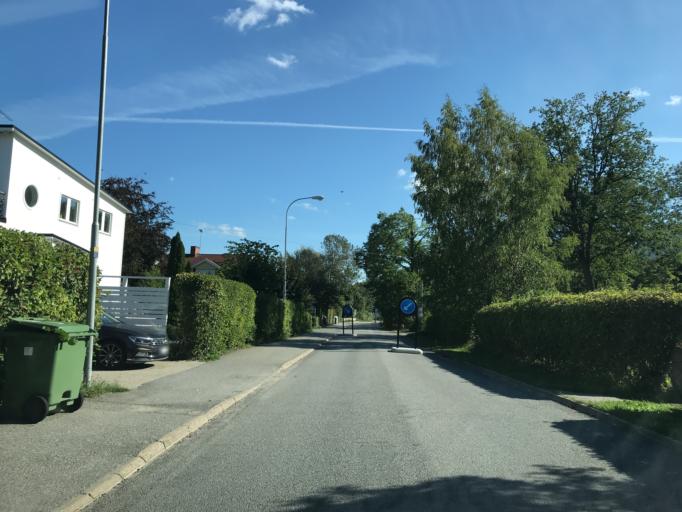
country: SE
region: Stockholm
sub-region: Sollentuna Kommun
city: Sollentuna
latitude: 59.4139
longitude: 17.9837
